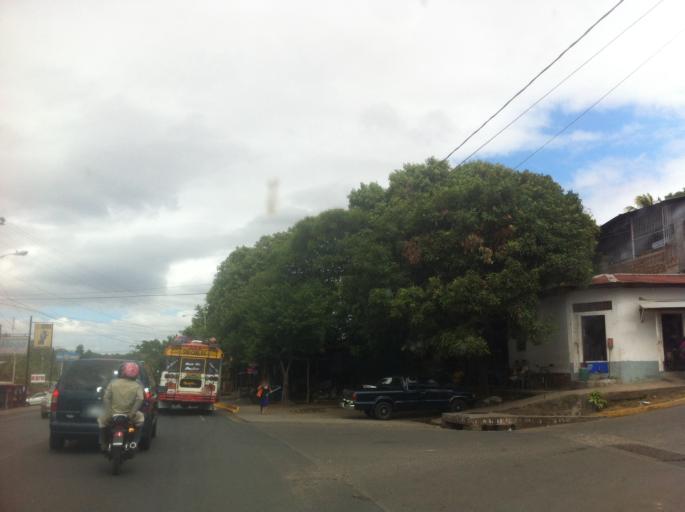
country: NI
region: Chontales
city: Juigalpa
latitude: 12.1047
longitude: -85.3678
